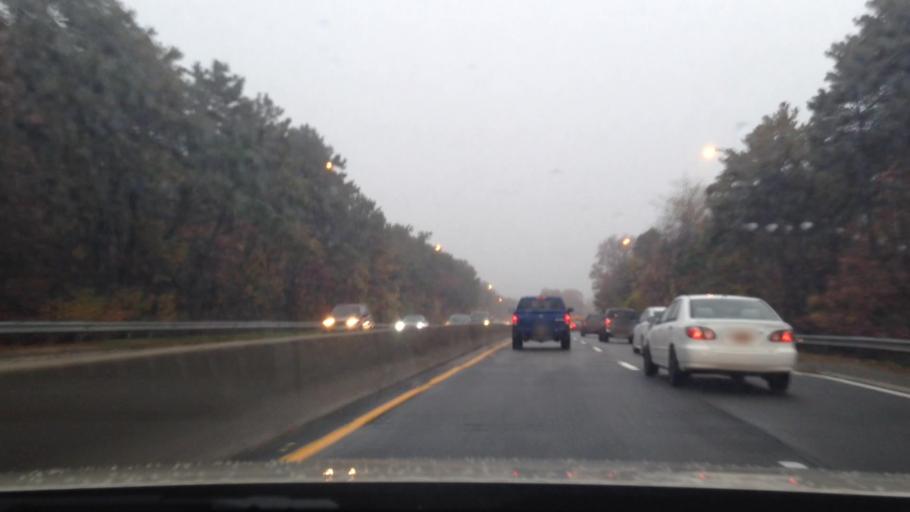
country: US
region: New York
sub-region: Suffolk County
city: Bay Wood
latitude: 40.7729
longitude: -73.2800
